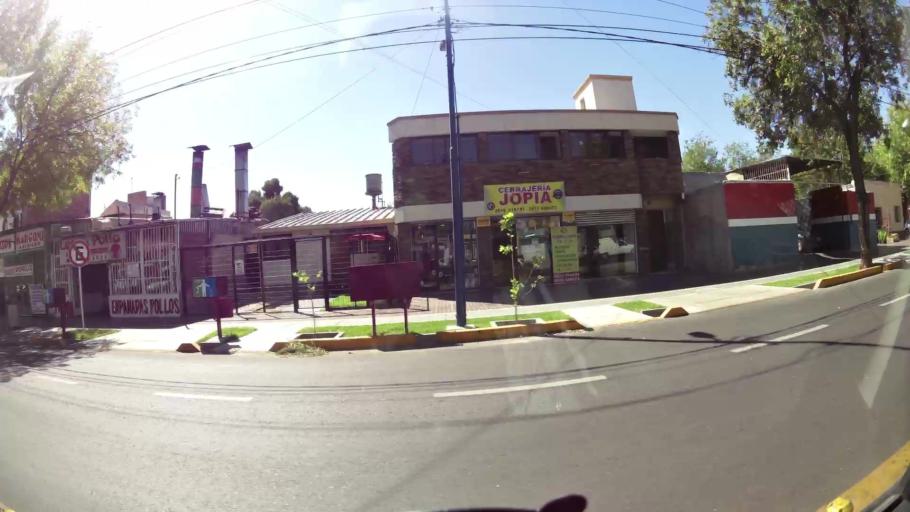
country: AR
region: Mendoza
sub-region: Departamento de Godoy Cruz
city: Godoy Cruz
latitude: -32.9052
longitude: -68.8602
